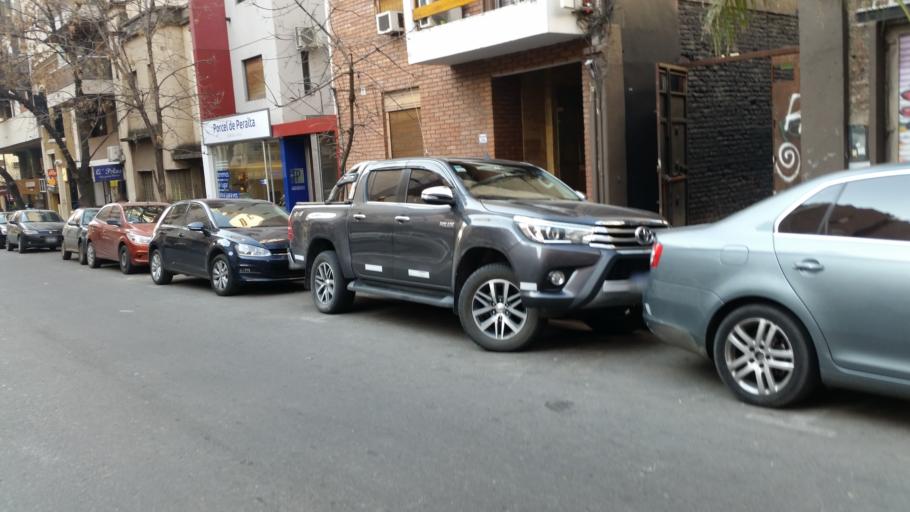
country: AR
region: Cordoba
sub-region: Departamento de Capital
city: Cordoba
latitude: -31.4280
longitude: -64.1891
